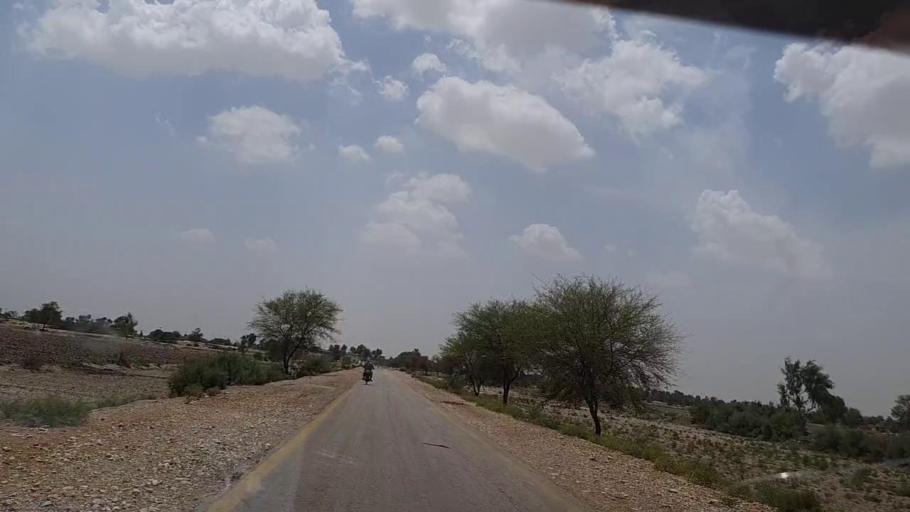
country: PK
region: Sindh
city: Bhan
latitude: 26.5417
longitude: 67.6396
